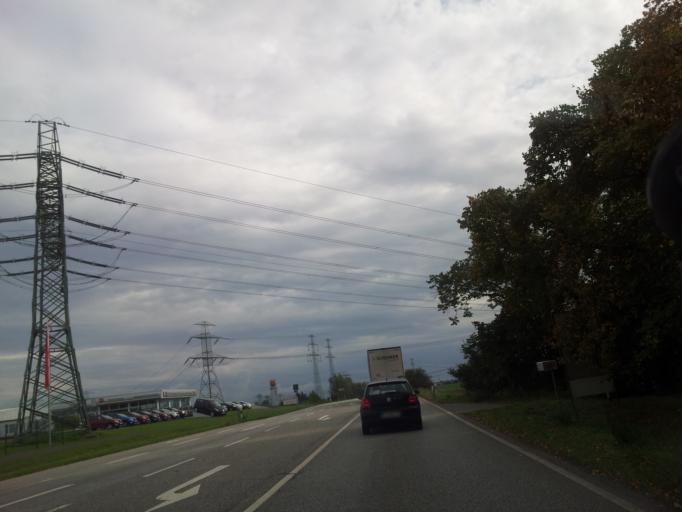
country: DE
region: Saxony-Anhalt
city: Wolmirstedt
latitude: 52.2757
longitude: 11.6283
